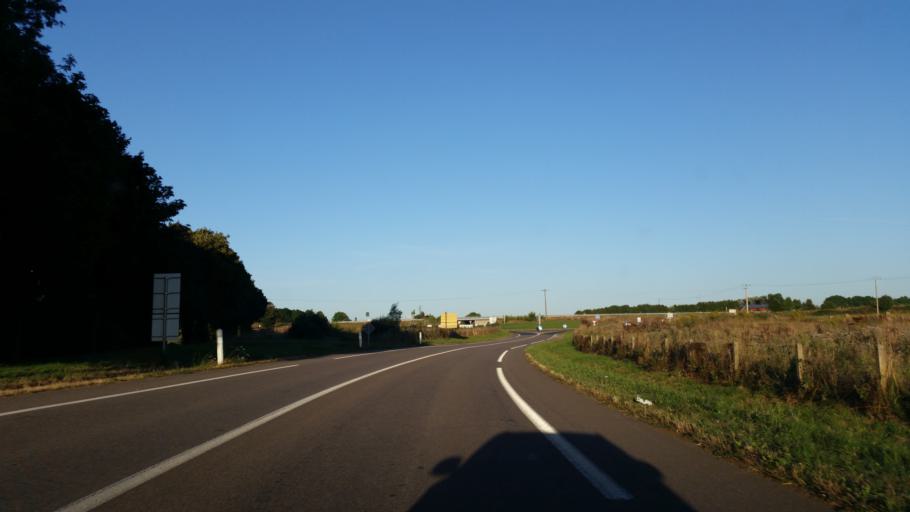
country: FR
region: Lower Normandy
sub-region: Departement du Calvados
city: Falaise
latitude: 48.8869
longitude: -0.2252
